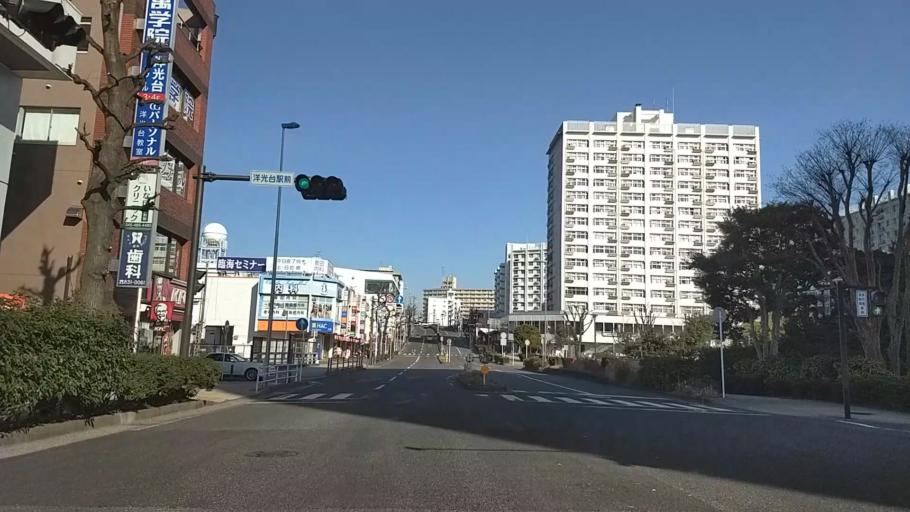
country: JP
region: Kanagawa
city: Kamakura
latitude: 35.3779
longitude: 139.5958
